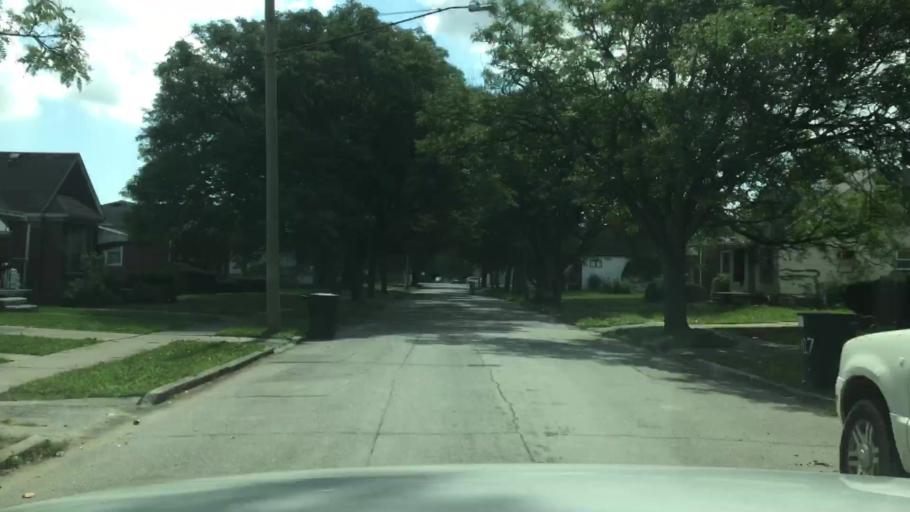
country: US
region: Michigan
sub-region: Wayne County
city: Dearborn Heights
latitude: 42.3452
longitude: -83.2232
